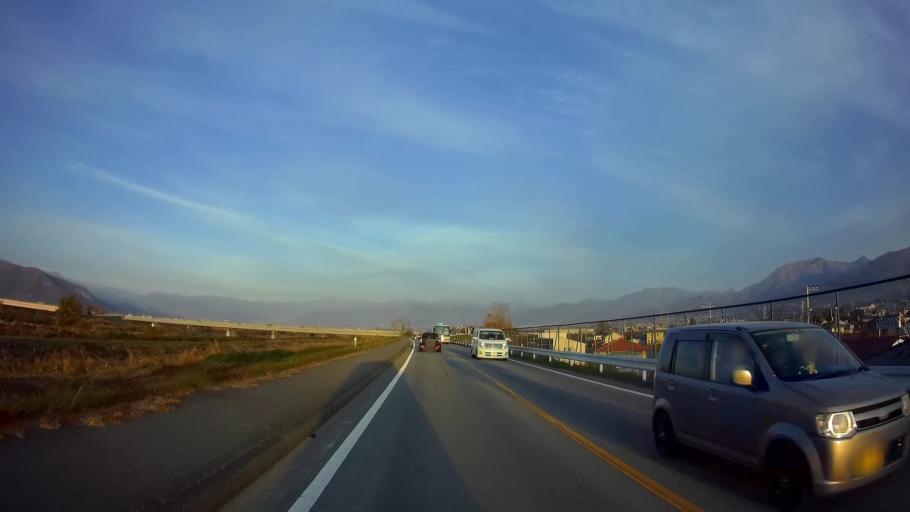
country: JP
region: Yamanashi
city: Isawa
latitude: 35.6108
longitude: 138.5980
